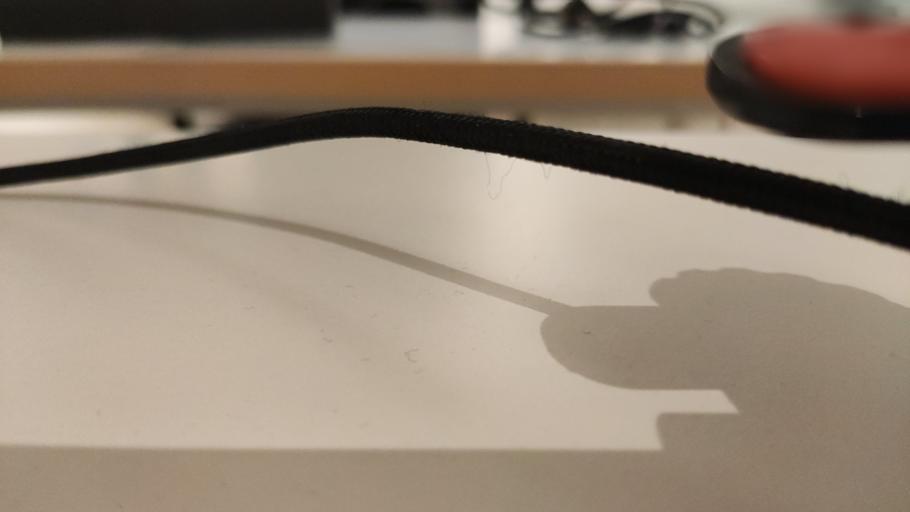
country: RU
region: Moskovskaya
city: Dorokhovo
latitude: 55.4555
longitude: 36.3531
